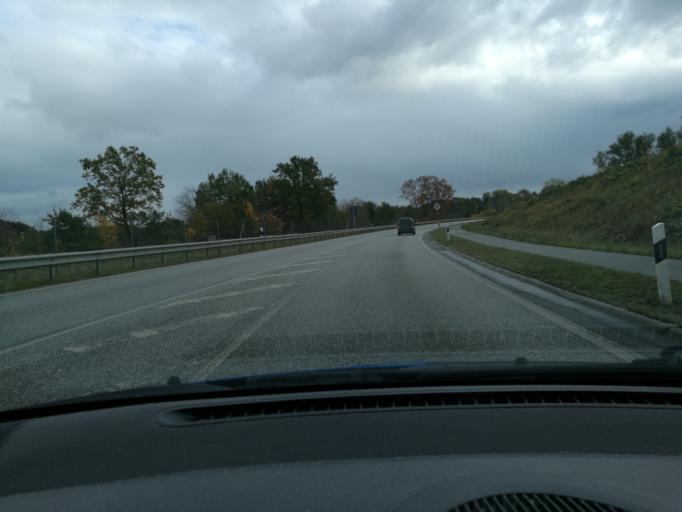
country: DE
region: Schleswig-Holstein
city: Pogeez
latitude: 53.7425
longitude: 10.7296
